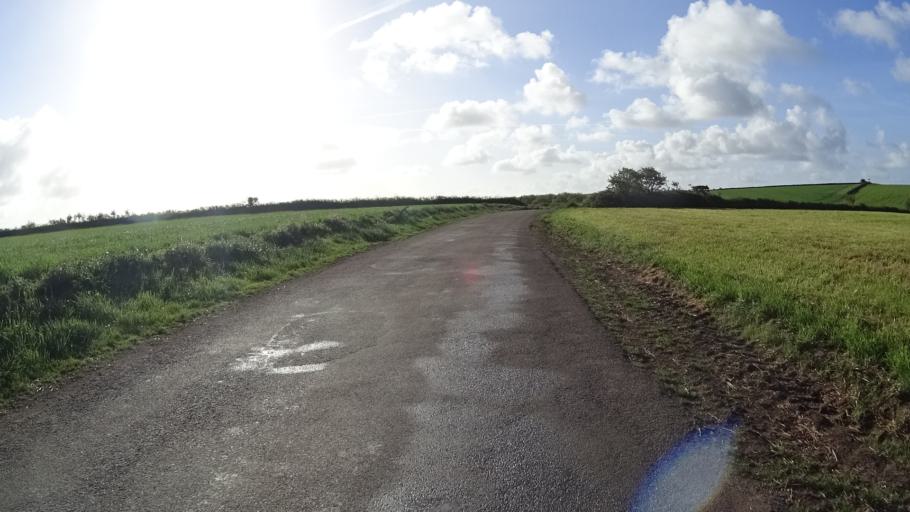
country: FR
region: Brittany
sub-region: Departement du Finistere
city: Ploumoguer
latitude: 48.4240
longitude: -4.7017
